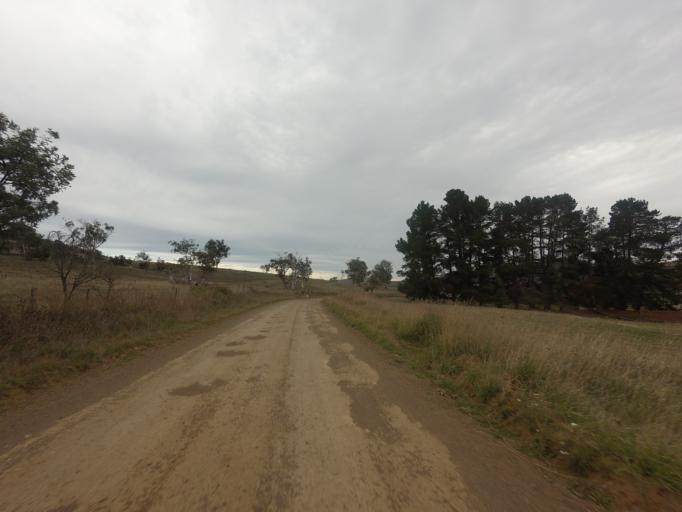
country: AU
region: Tasmania
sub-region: Derwent Valley
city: New Norfolk
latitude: -42.5425
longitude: 146.9493
